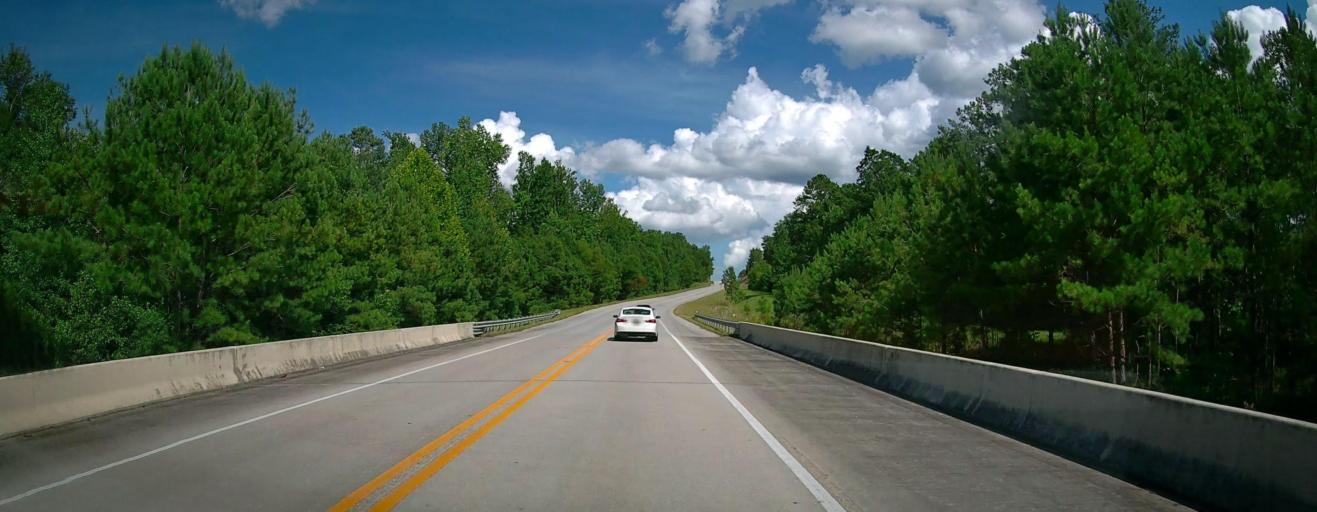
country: US
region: Alabama
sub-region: Lee County
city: Auburn
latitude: 32.4323
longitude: -85.4678
